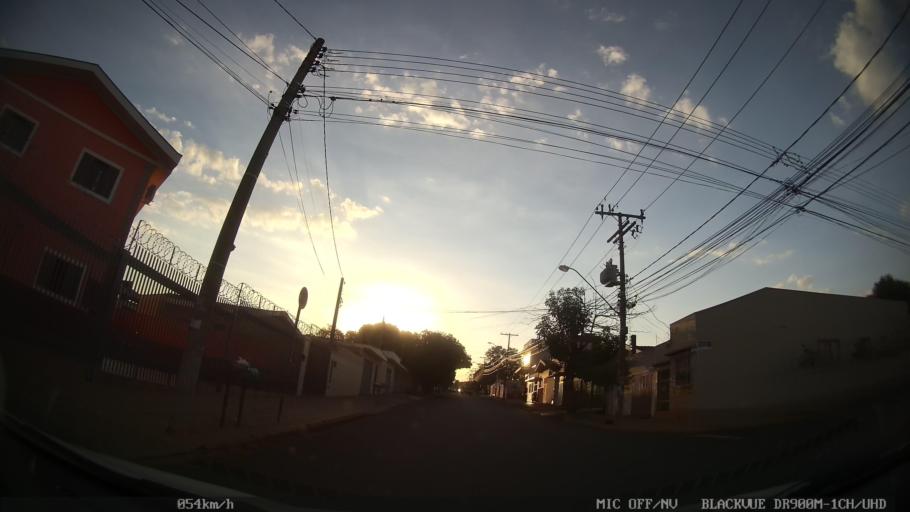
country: BR
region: Sao Paulo
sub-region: Ribeirao Preto
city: Ribeirao Preto
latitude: -21.1635
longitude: -47.8298
